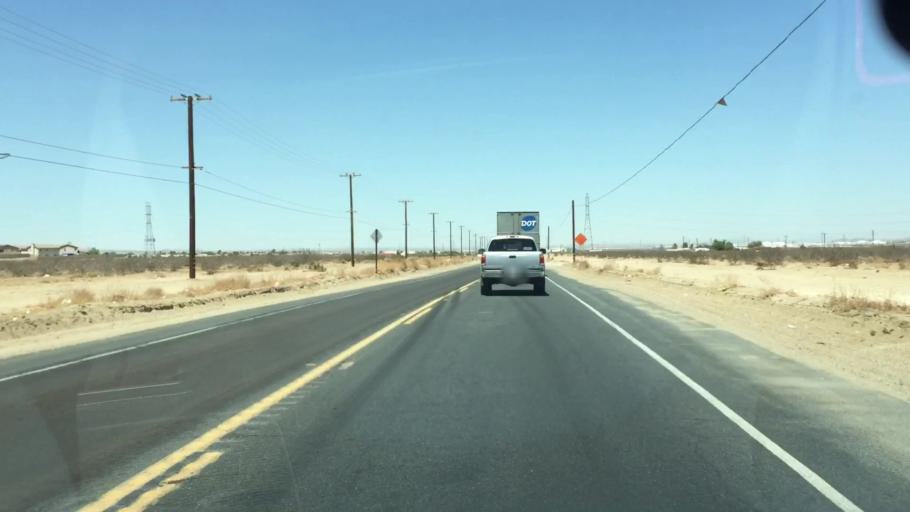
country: US
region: California
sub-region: San Bernardino County
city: Mountain View Acres
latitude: 34.5160
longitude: -117.3994
